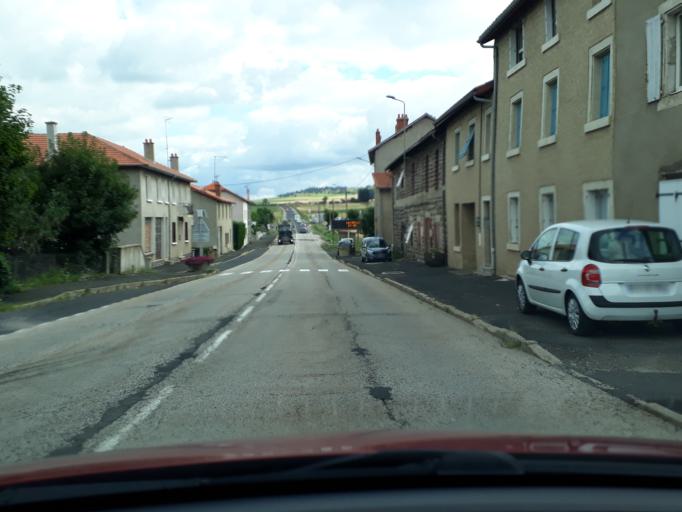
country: FR
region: Auvergne
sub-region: Departement de la Haute-Loire
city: Solignac-sur-Loire
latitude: 44.8911
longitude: 3.8483
